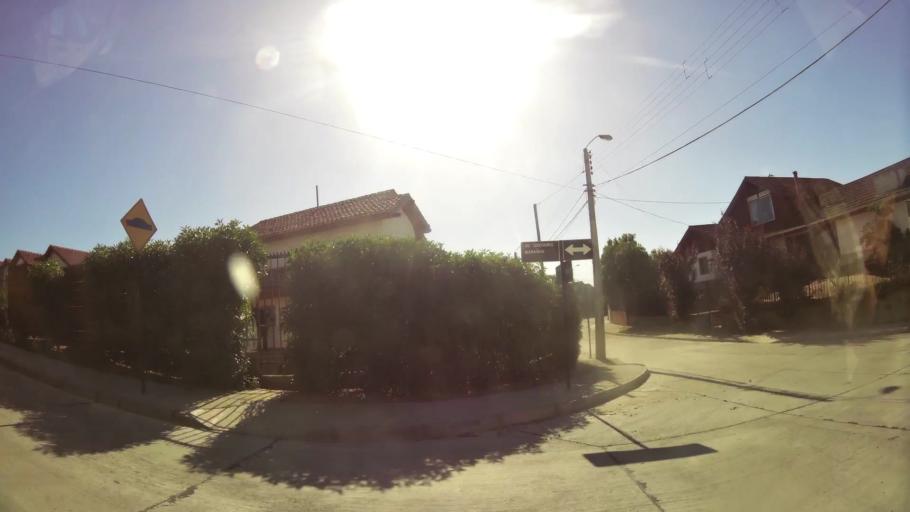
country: CL
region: Valparaiso
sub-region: Provincia de Valparaiso
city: Vina del Mar
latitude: -33.0374
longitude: -71.5564
